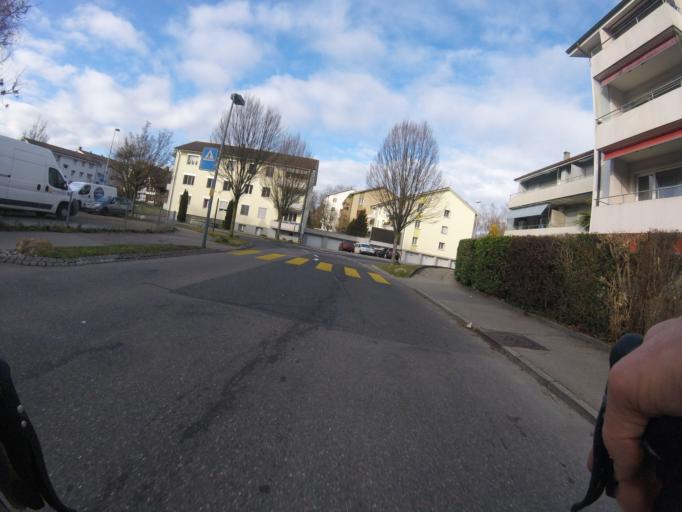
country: CH
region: Bern
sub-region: Bern-Mittelland District
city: Bolligen
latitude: 46.9548
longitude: 7.4899
